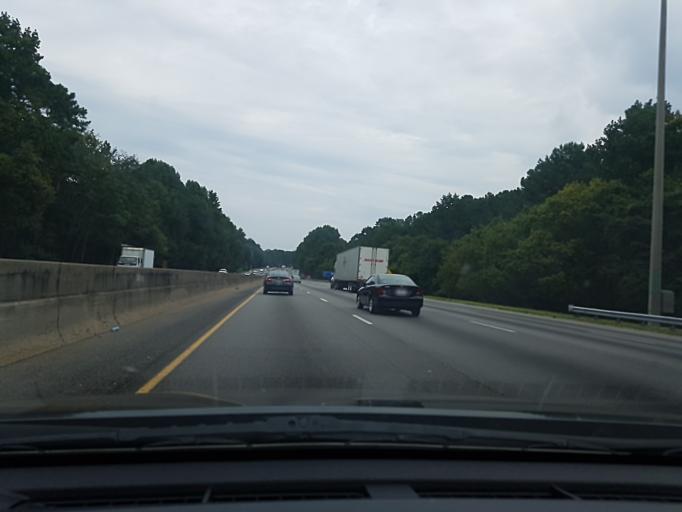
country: US
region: Georgia
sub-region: DeKalb County
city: Panthersville
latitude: 33.6949
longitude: -84.2886
